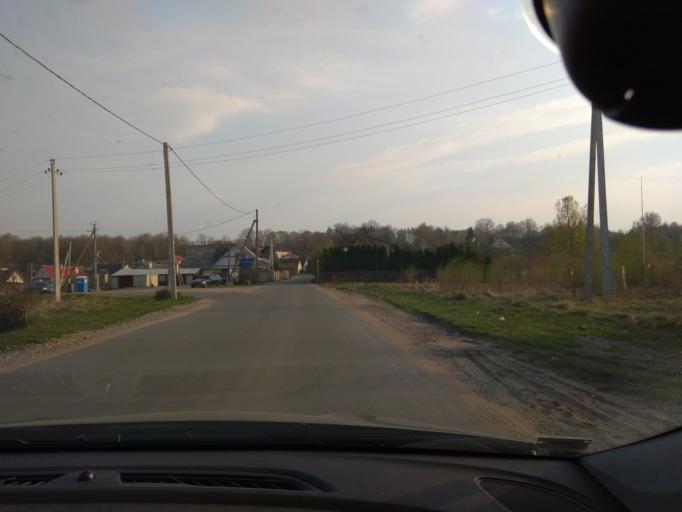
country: LT
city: Baltoji Voke
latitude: 54.5964
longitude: 25.1755
